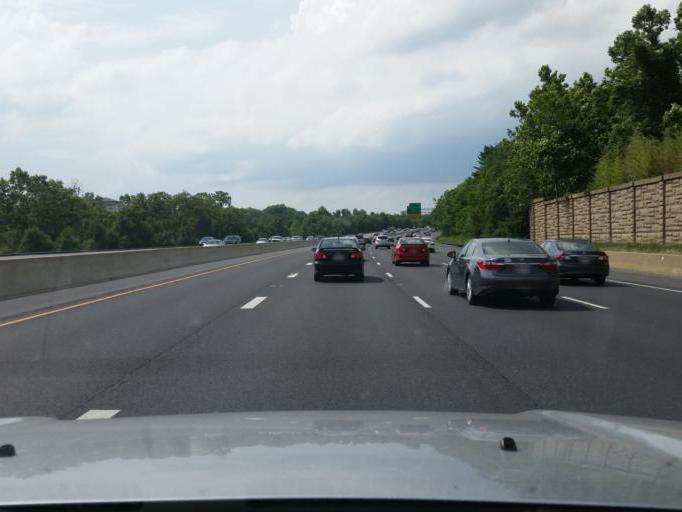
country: US
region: Maryland
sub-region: Montgomery County
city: Germantown
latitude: 39.1649
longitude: -77.2393
